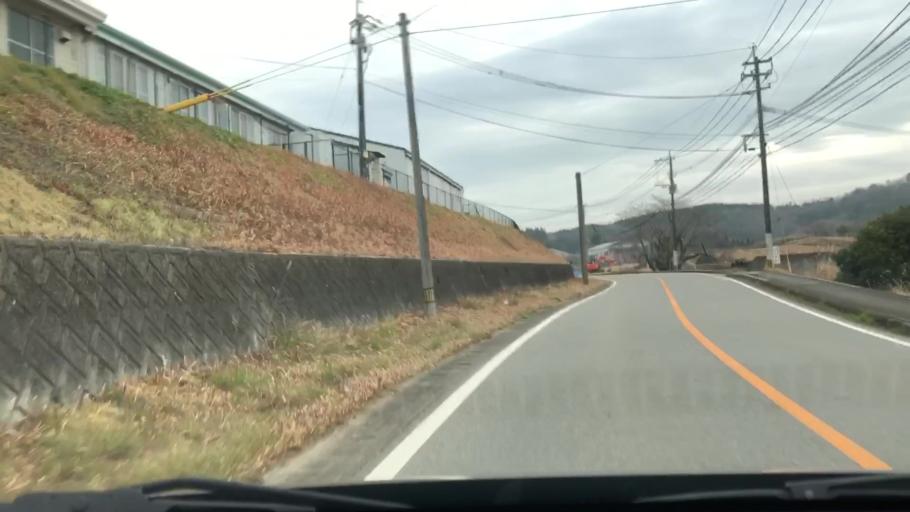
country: JP
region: Oita
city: Usuki
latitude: 33.0189
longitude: 131.6727
